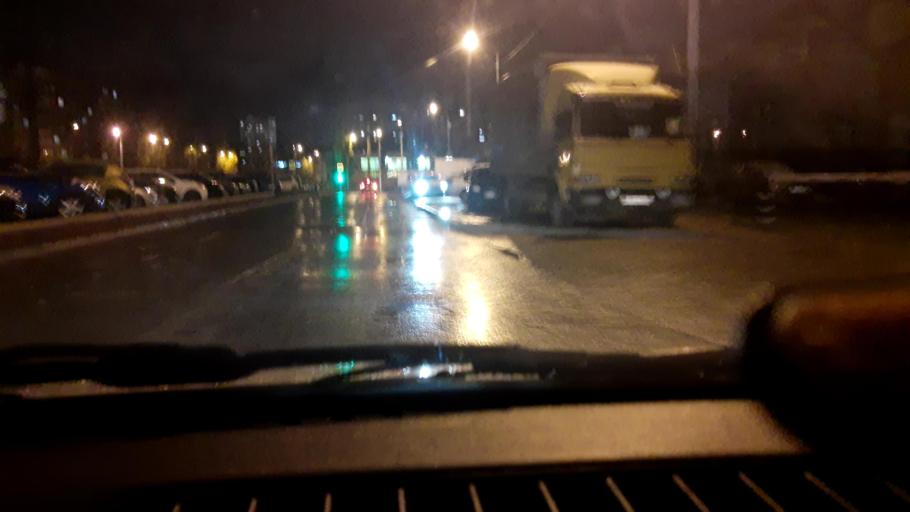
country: RU
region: Bashkortostan
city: Ufa
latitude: 54.7634
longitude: 56.0567
